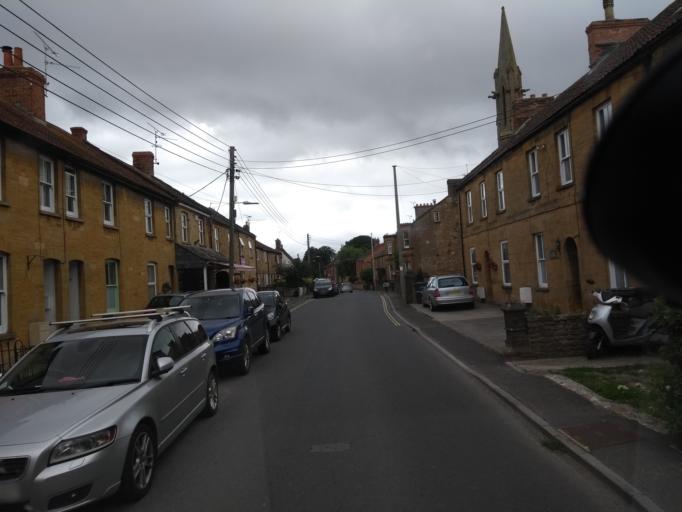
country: GB
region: England
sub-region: Somerset
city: Martock
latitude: 50.9746
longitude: -2.7671
